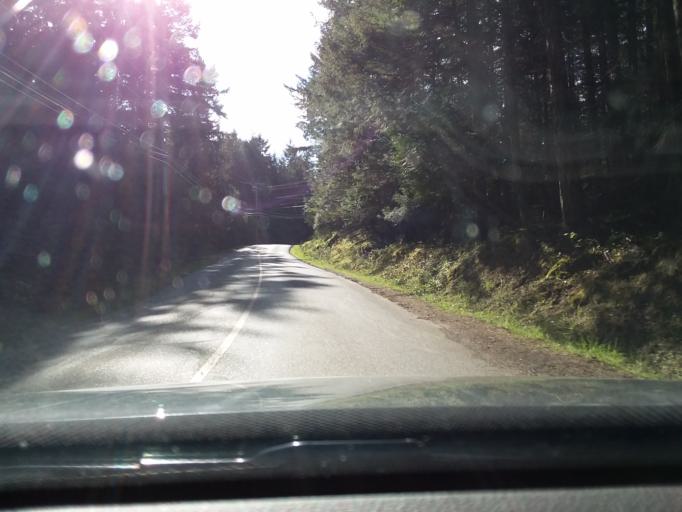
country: CA
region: British Columbia
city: North Saanich
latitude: 48.8858
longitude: -123.3327
